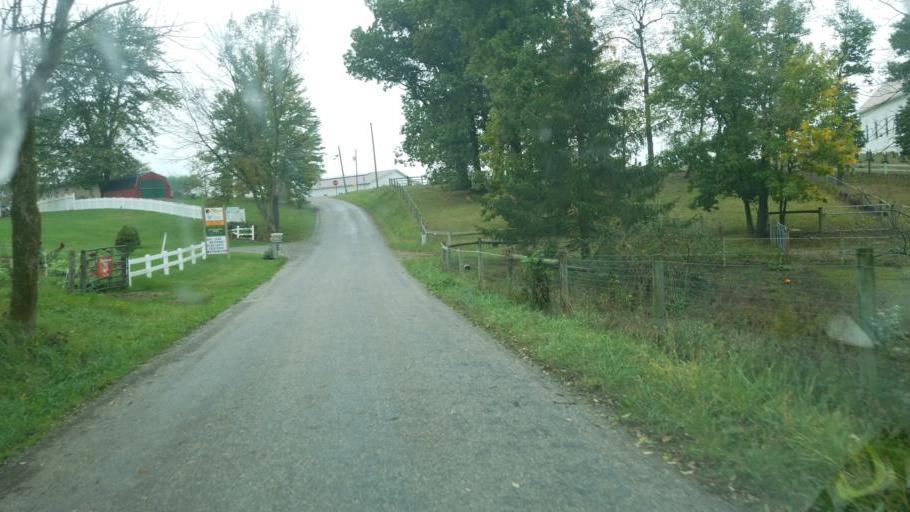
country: US
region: Ohio
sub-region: Tuscarawas County
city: Sugarcreek
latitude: 40.5768
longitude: -81.7075
